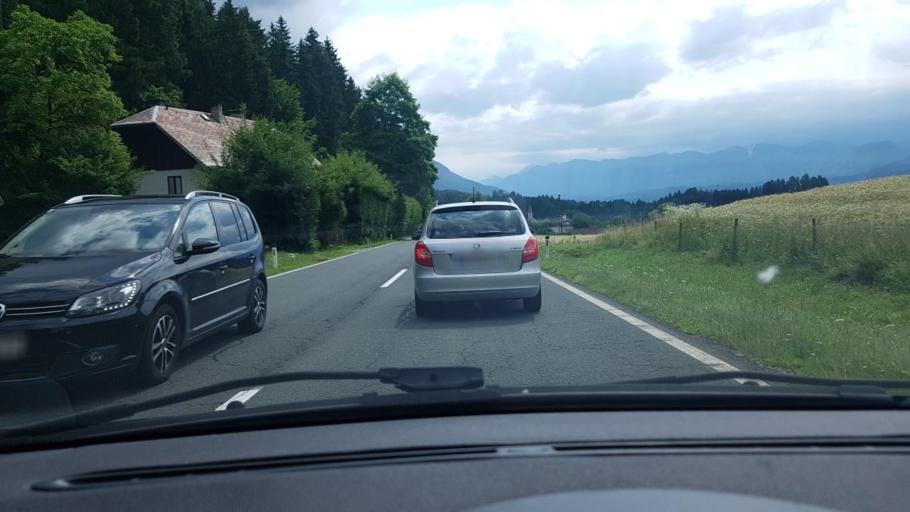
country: AT
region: Carinthia
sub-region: Politischer Bezirk Villach Land
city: Feistritz an der Gail
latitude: 46.6070
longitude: 13.5456
